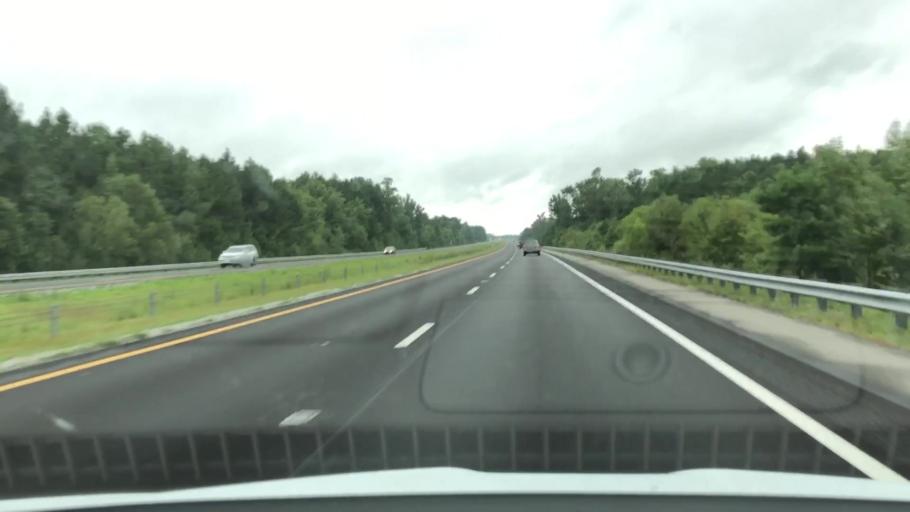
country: US
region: North Carolina
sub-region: Wayne County
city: Goldsboro
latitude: 35.4534
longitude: -77.9844
